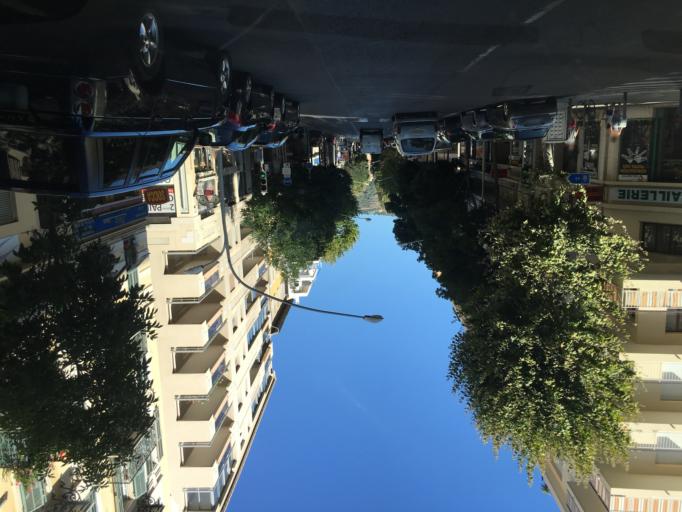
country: FR
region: Provence-Alpes-Cote d'Azur
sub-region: Departement des Alpes-Maritimes
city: Villefranche-sur-Mer
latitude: 43.7012
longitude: 7.2881
